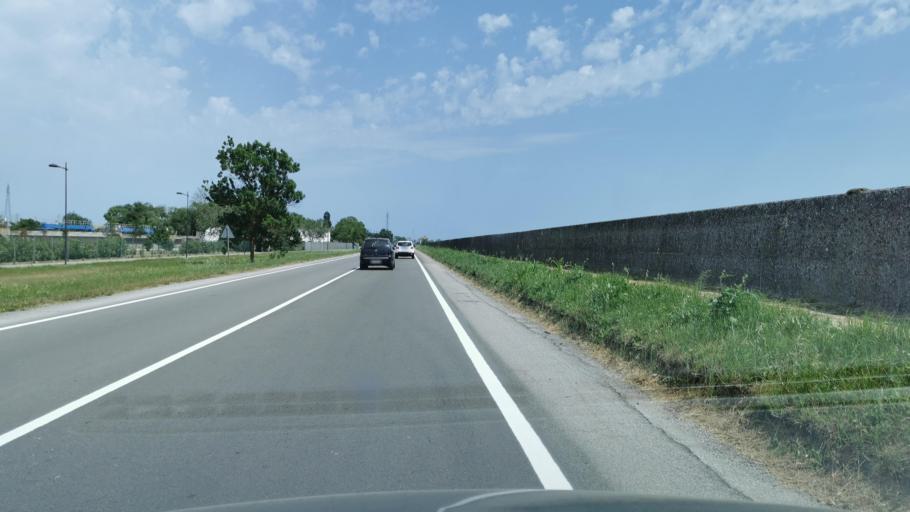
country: IT
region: Emilia-Romagna
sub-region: Provincia di Ferrara
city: Comacchio
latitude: 44.6777
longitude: 12.2061
